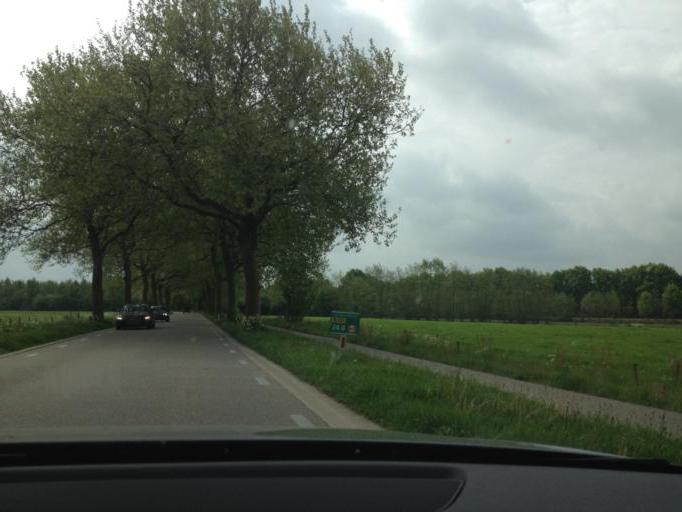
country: NL
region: Gelderland
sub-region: Gemeente Barneveld
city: Terschuur
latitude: 52.1753
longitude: 5.5487
